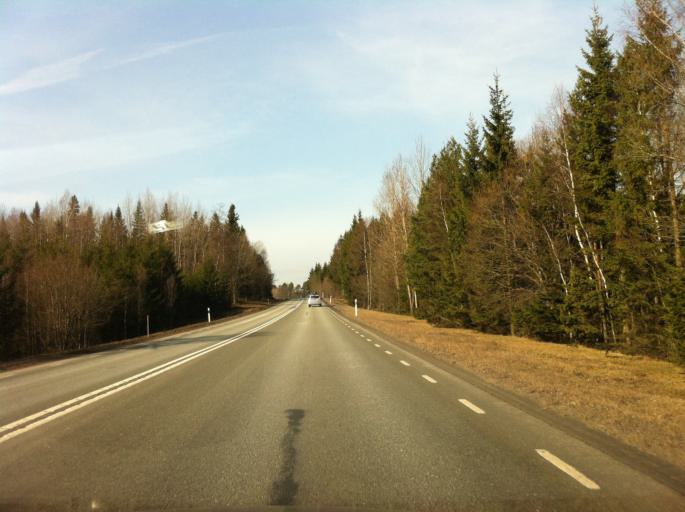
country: SE
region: Joenkoeping
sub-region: Jonkopings Kommun
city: Bankeryd
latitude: 57.8393
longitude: 14.0657
